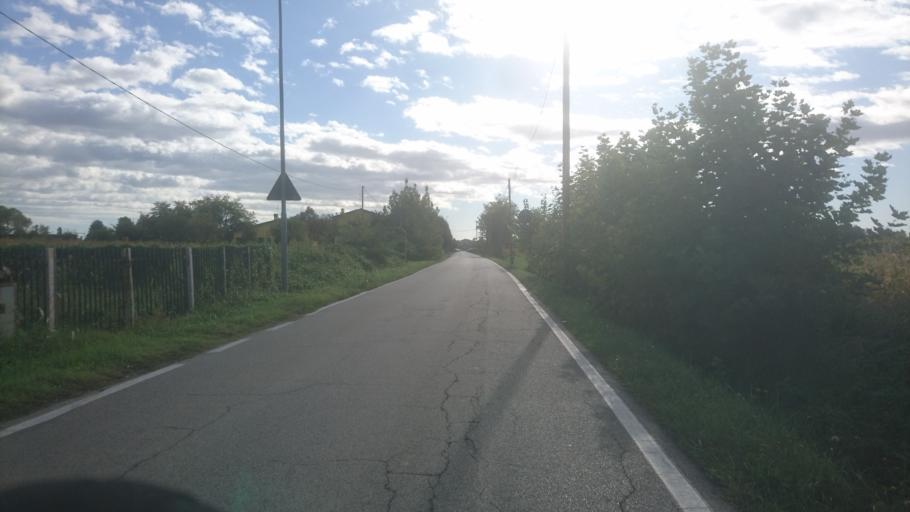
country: IT
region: Veneto
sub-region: Provincia di Padova
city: Montegrotto Terme
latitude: 45.3420
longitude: 11.8058
